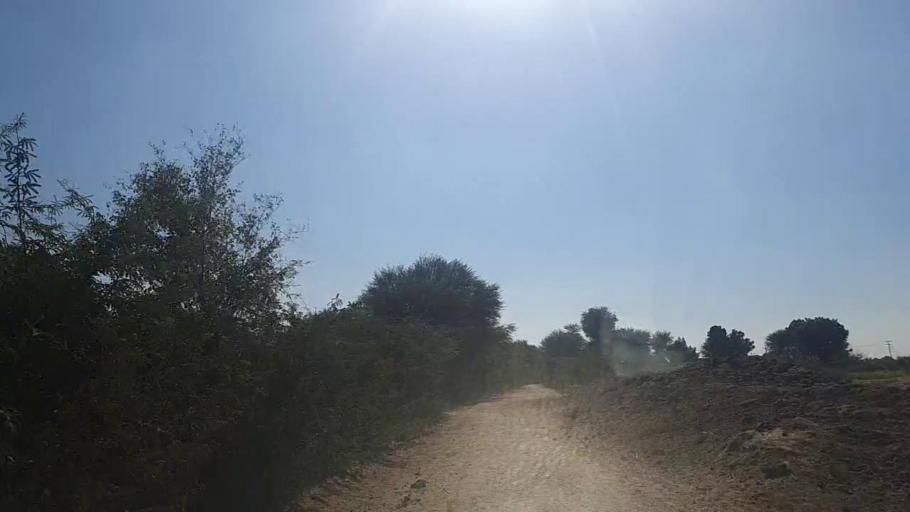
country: PK
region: Sindh
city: Khadro
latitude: 26.1557
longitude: 68.8380
